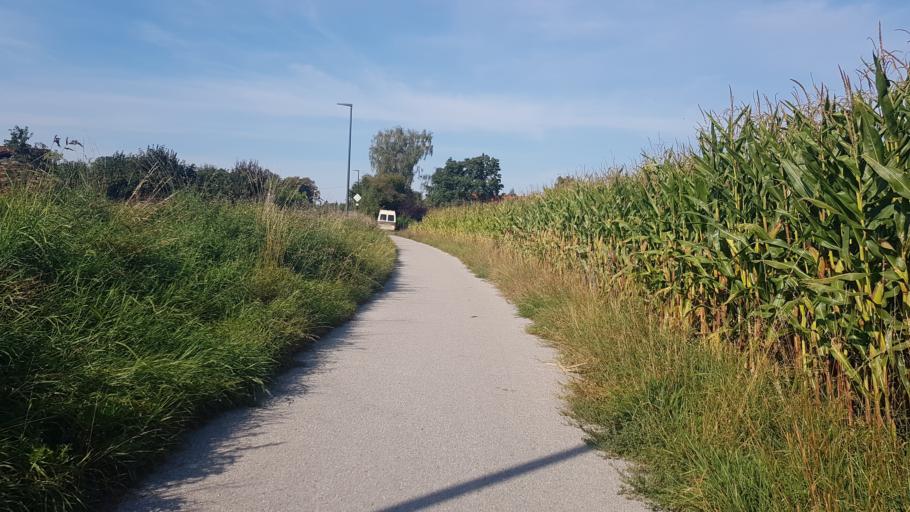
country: DE
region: Bavaria
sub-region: Upper Bavaria
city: Wessling
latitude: 48.0775
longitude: 11.2655
